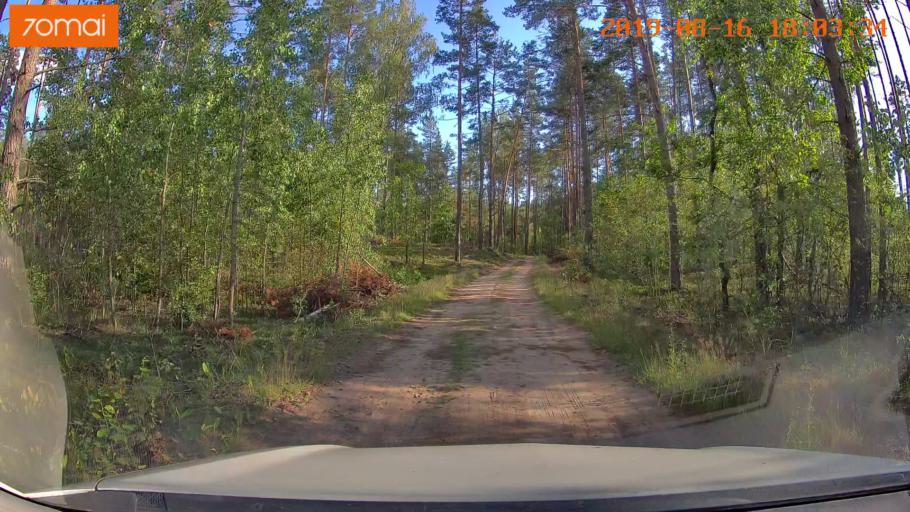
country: BY
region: Mogilev
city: Asipovichy
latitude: 53.2195
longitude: 28.6553
